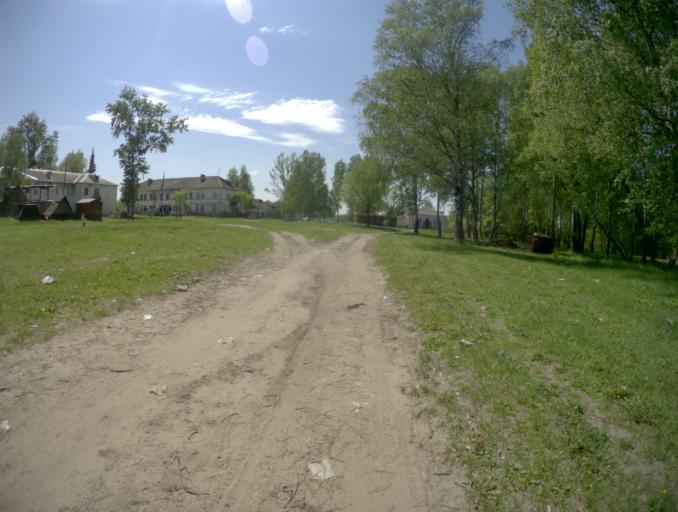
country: RU
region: Vladimir
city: Gusevskiy
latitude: 55.6692
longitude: 40.4779
